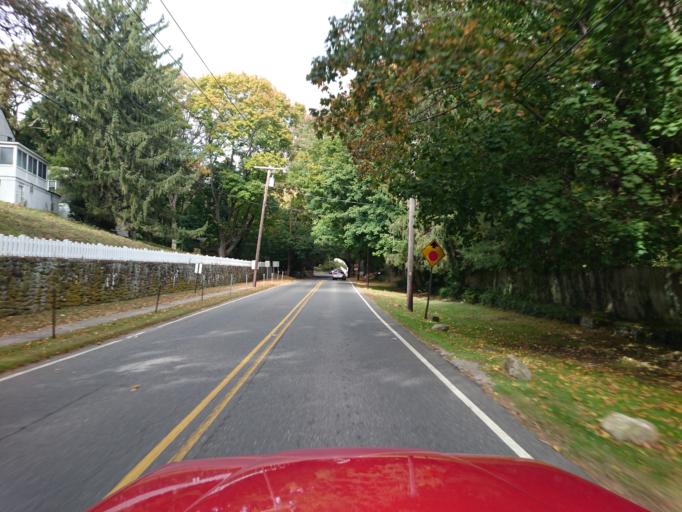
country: US
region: New York
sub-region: Nassau County
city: Locust Valley
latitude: 40.8750
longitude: -73.5952
